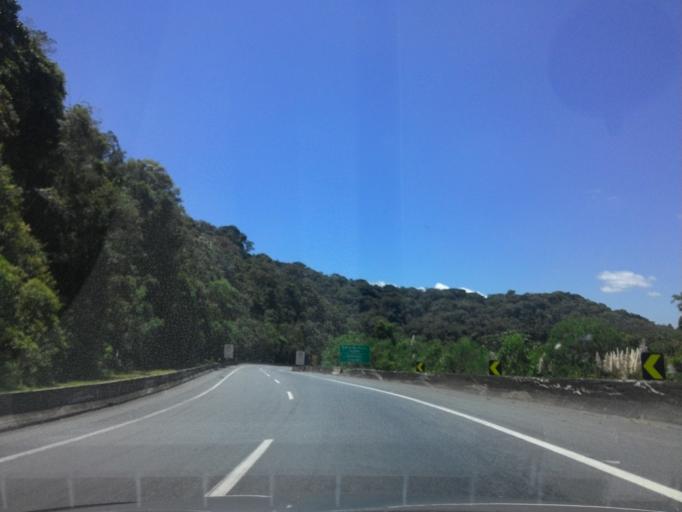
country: BR
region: Sao Paulo
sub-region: Cajati
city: Cajati
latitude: -24.9652
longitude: -48.4319
